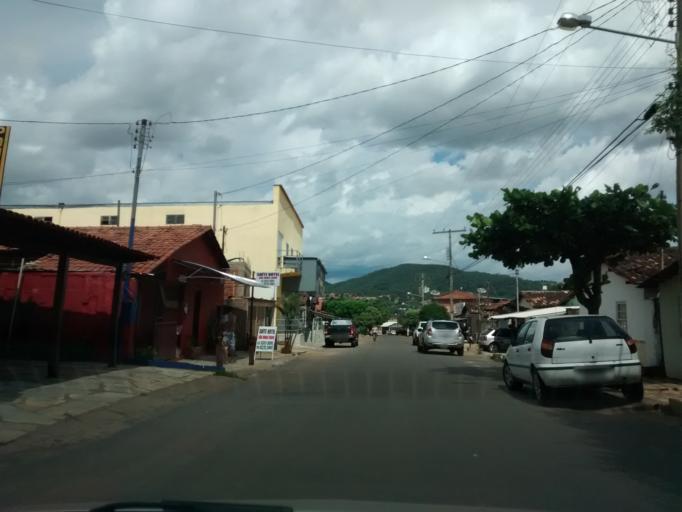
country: BR
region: Goias
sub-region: Pirenopolis
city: Pirenopolis
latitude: -15.8450
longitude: -48.9616
